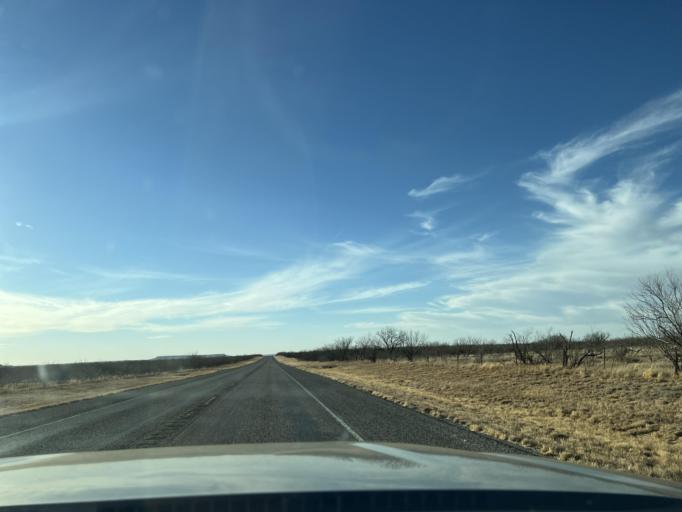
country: US
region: Texas
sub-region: Borden County
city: Gail
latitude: 32.7676
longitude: -101.3039
